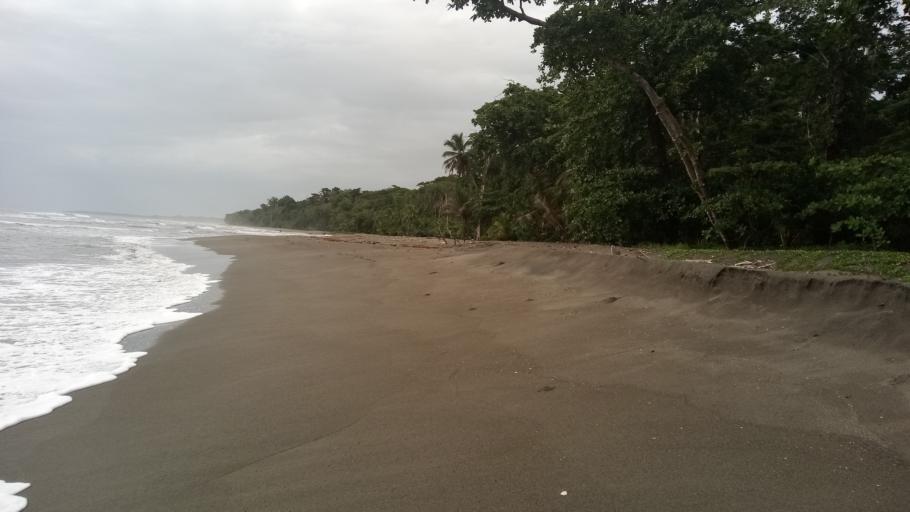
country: CR
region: Limon
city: Sixaola
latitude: 9.6157
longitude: -82.6201
